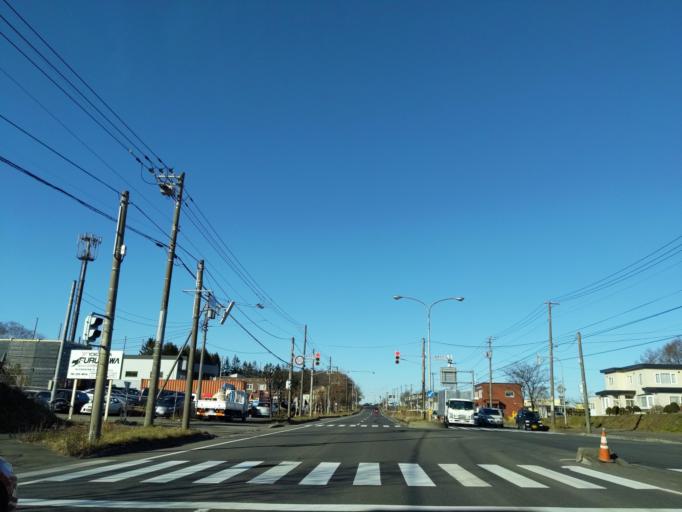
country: JP
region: Hokkaido
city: Kitahiroshima
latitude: 42.9431
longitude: 141.5029
